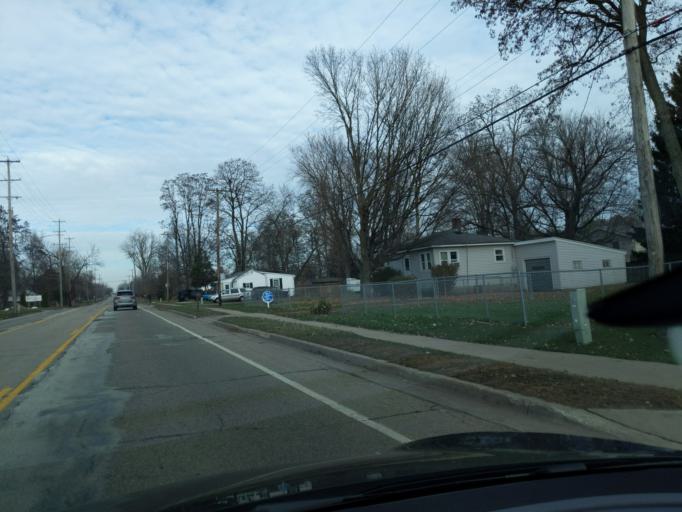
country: US
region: Michigan
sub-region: Ingham County
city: Holt
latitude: 42.6569
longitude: -84.5235
